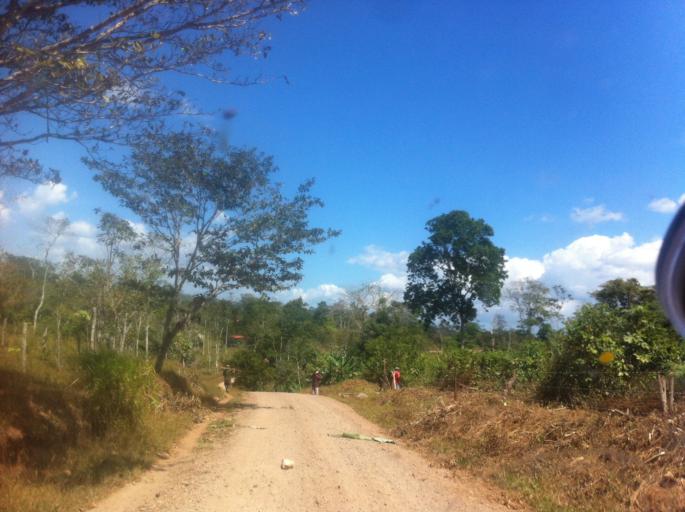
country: CR
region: Alajuela
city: Los Chiles
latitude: 11.2482
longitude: -84.4635
